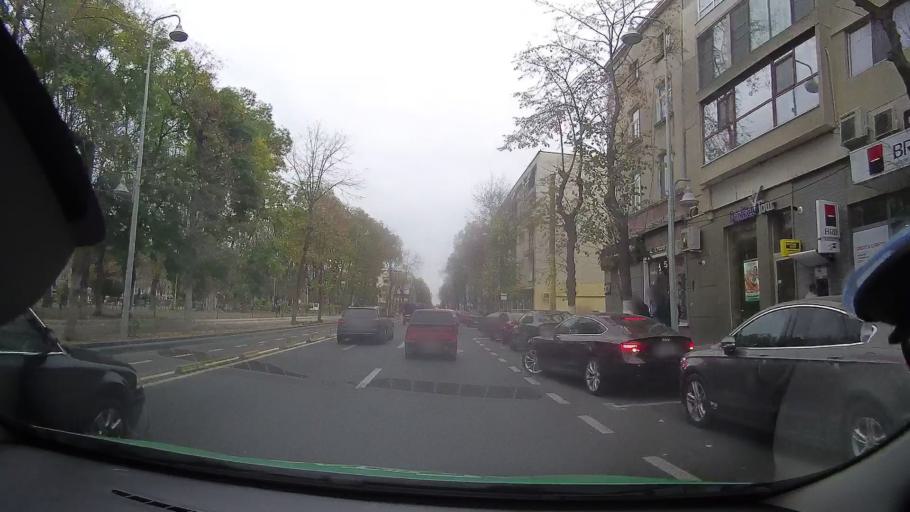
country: RO
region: Constanta
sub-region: Municipiul Constanta
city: Constanta
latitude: 44.1815
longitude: 28.6488
